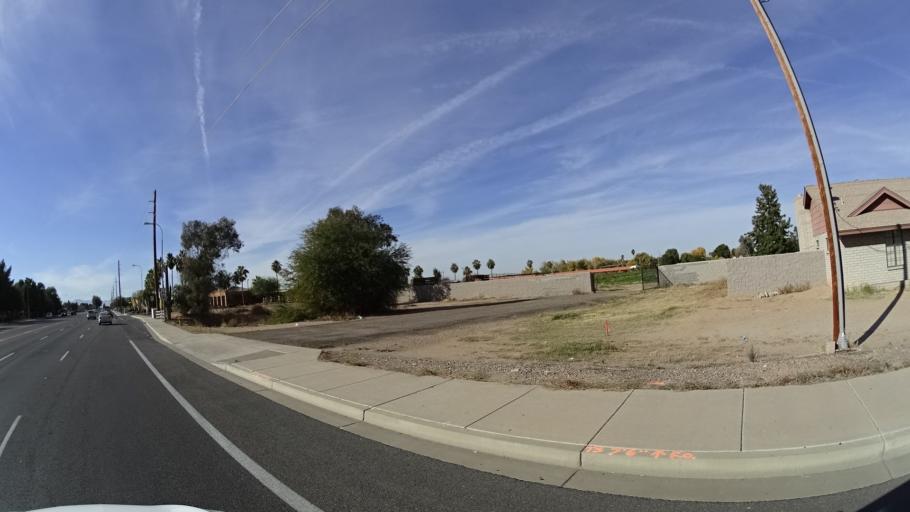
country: US
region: Arizona
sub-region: Maricopa County
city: Sun Lakes
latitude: 33.2190
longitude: -111.8167
